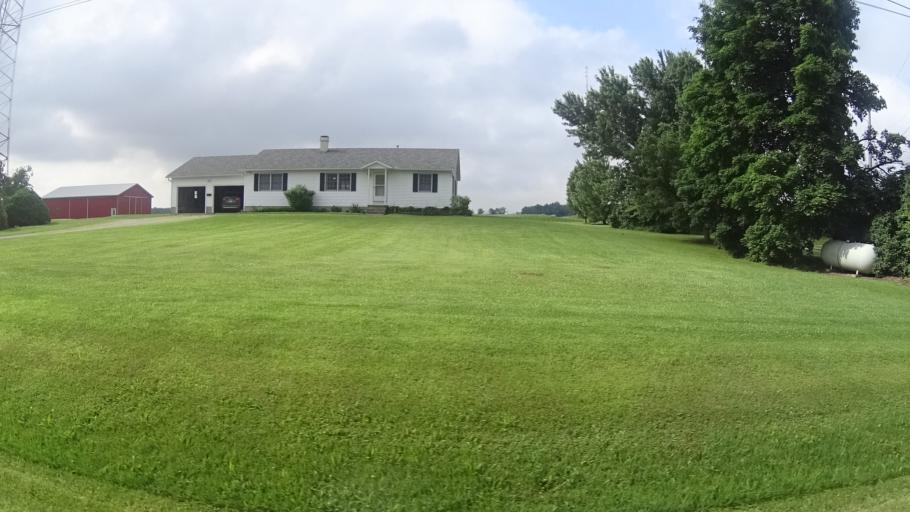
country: US
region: Ohio
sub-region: Huron County
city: Wakeman
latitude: 41.3051
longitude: -82.4870
